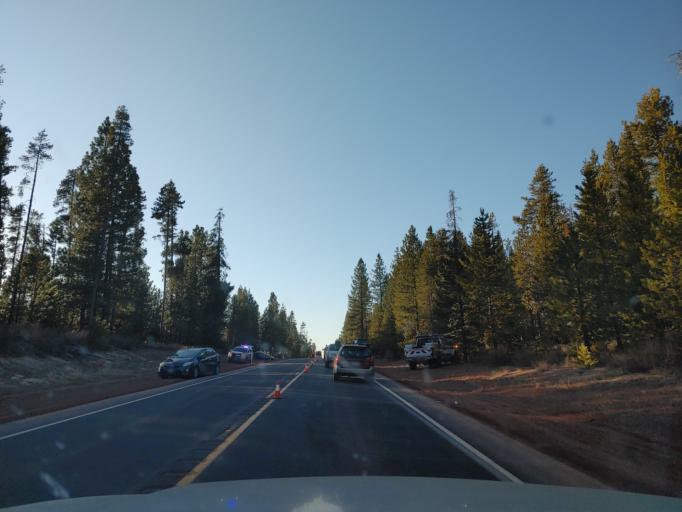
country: US
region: Oregon
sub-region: Deschutes County
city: La Pine
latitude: 43.3817
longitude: -121.8024
